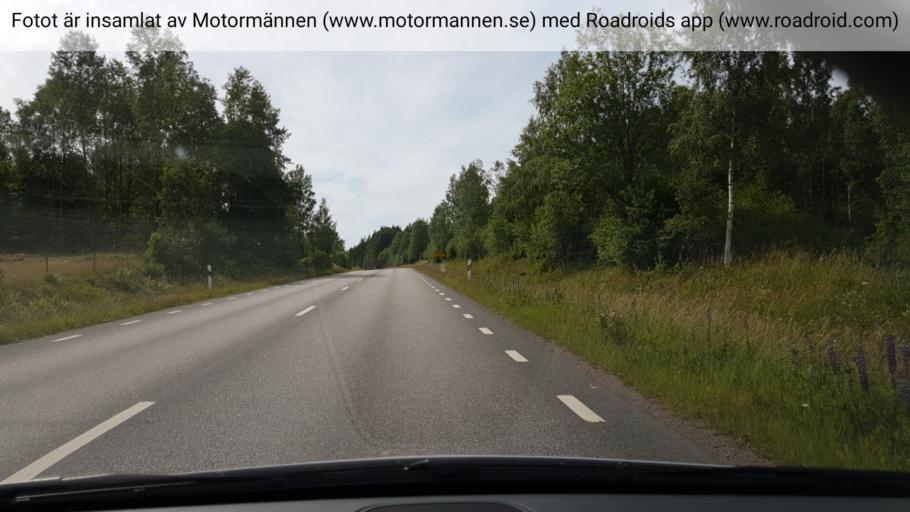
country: SE
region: Vaestra Goetaland
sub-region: Tibro Kommun
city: Tibro
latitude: 58.3420
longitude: 14.1830
